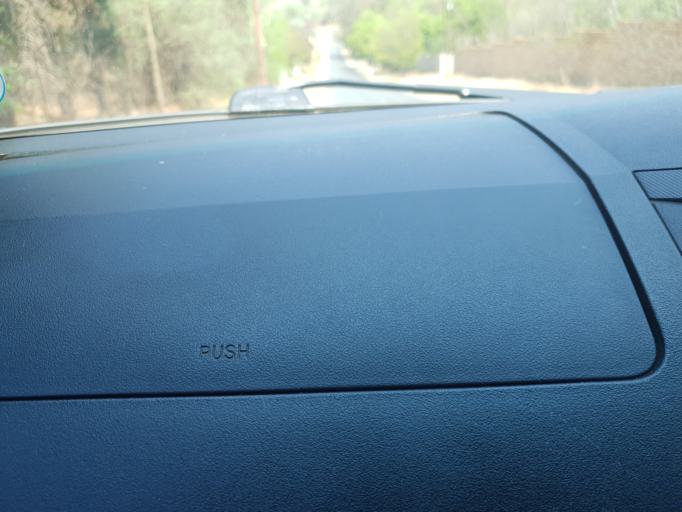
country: ZA
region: Gauteng
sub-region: City of Johannesburg Metropolitan Municipality
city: Midrand
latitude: -25.9879
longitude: 28.0949
